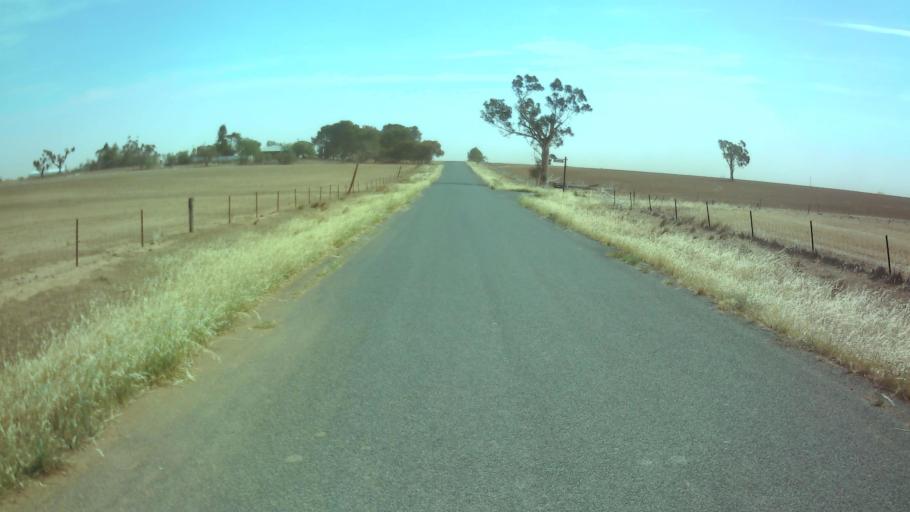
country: AU
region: New South Wales
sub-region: Weddin
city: Grenfell
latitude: -33.7330
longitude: 147.9976
